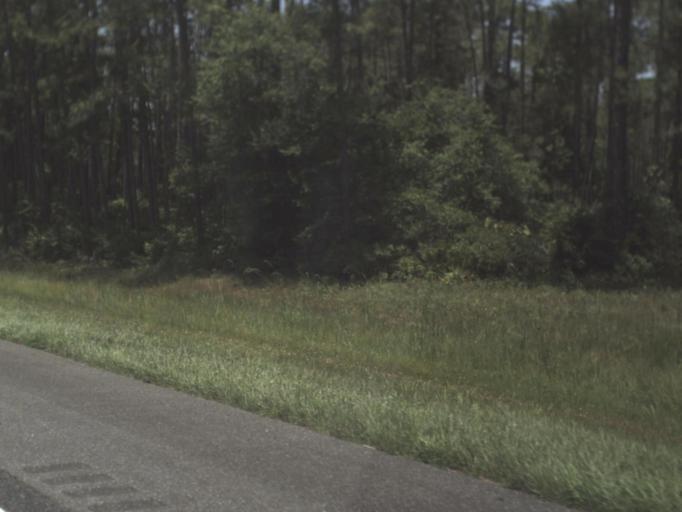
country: US
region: Florida
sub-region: Columbia County
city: Watertown
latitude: 30.2556
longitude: -82.4431
